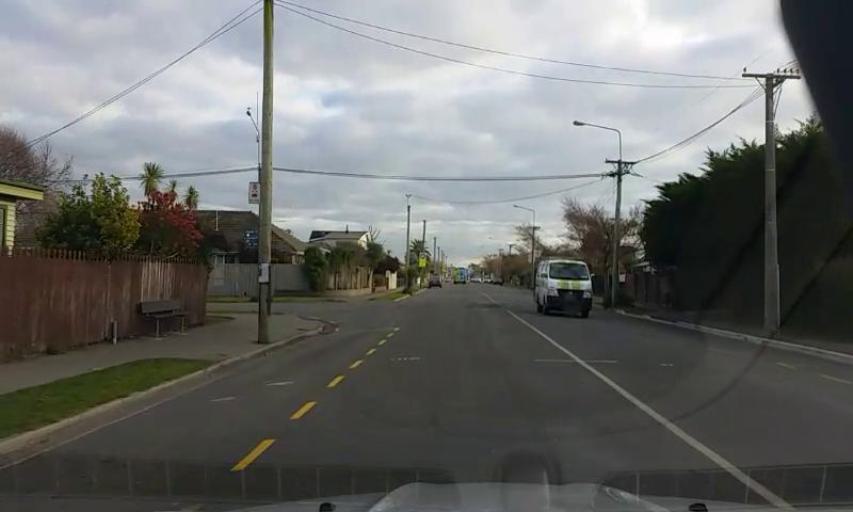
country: NZ
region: Canterbury
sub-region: Christchurch City
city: Christchurch
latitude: -43.5256
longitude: 172.7336
